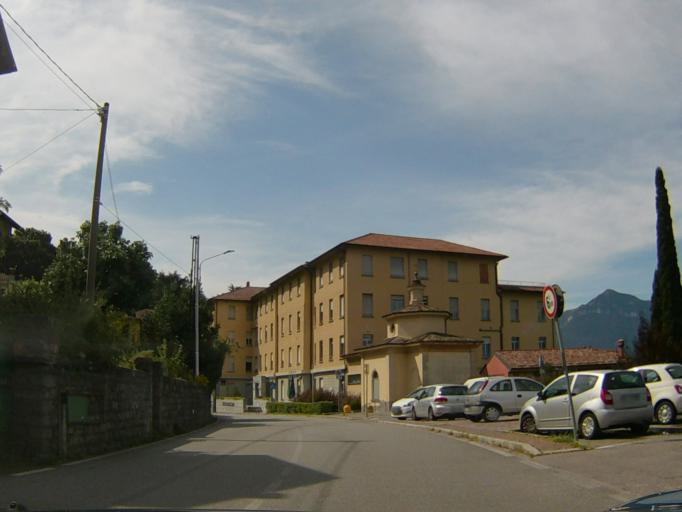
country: IT
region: Lombardy
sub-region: Provincia di Lecco
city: Bellano
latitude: 46.0492
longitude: 9.3076
